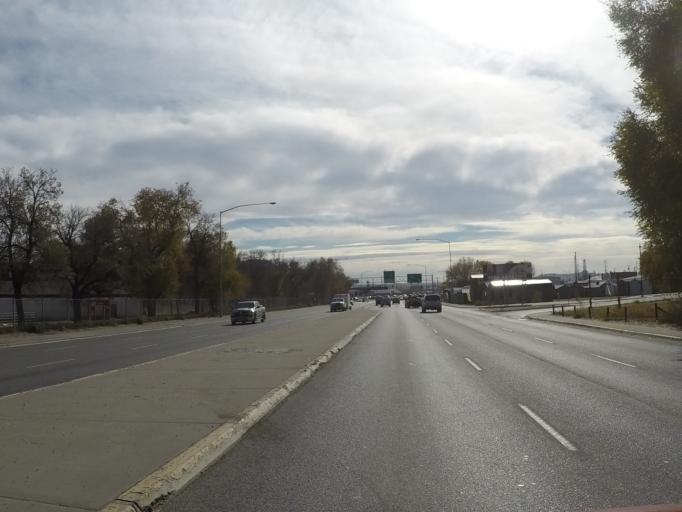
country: US
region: Montana
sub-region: Yellowstone County
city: Billings
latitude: 45.7969
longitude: -108.4815
